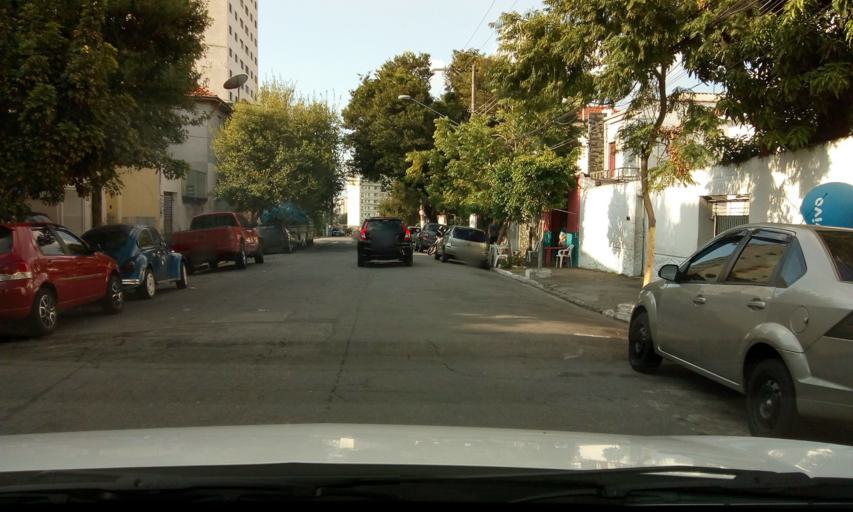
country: BR
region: Sao Paulo
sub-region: Sao Paulo
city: Sao Paulo
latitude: -23.5660
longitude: -46.6264
